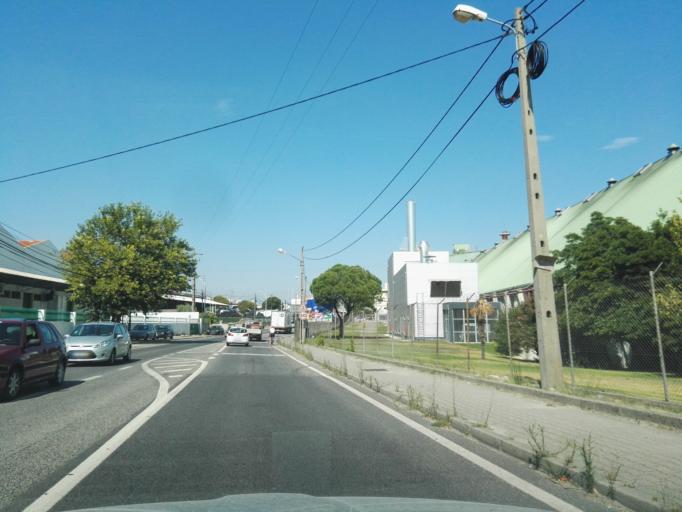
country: PT
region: Lisbon
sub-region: Loures
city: Santa Iria da Azoia
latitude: 38.8424
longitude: -9.0811
